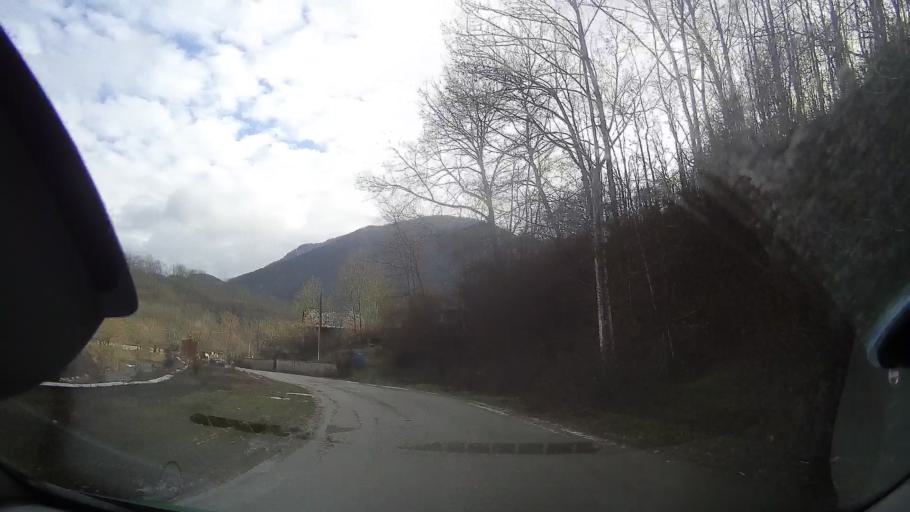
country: RO
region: Alba
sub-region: Comuna Ocolis
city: Ocolis
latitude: 46.4717
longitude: 23.4723
